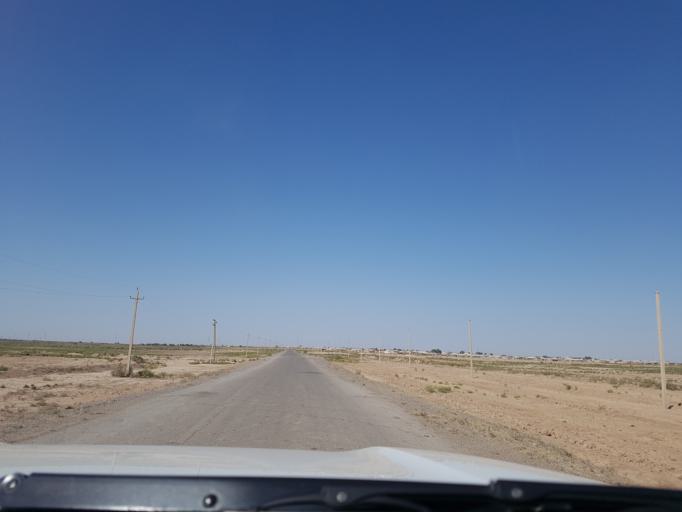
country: IR
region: Razavi Khorasan
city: Sarakhs
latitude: 36.4998
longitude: 61.2536
